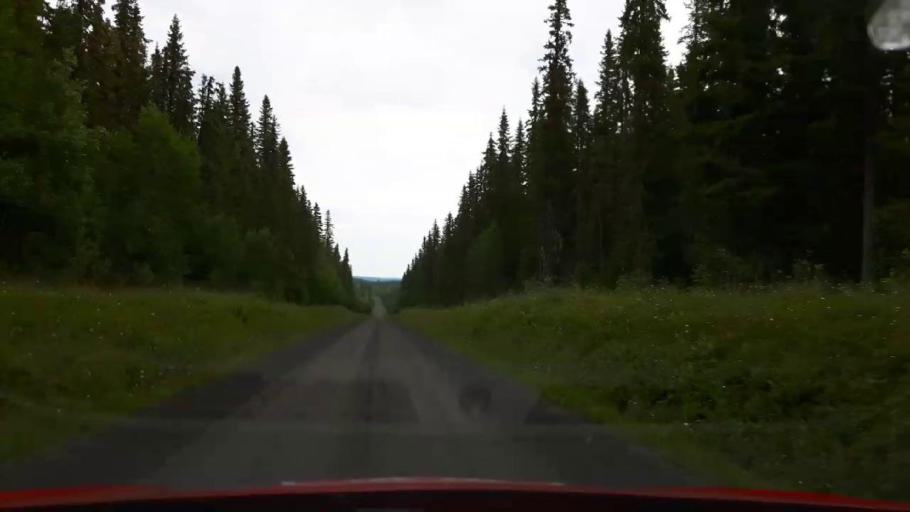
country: SE
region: Jaemtland
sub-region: OEstersunds Kommun
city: Lit
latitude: 63.3906
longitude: 15.2119
